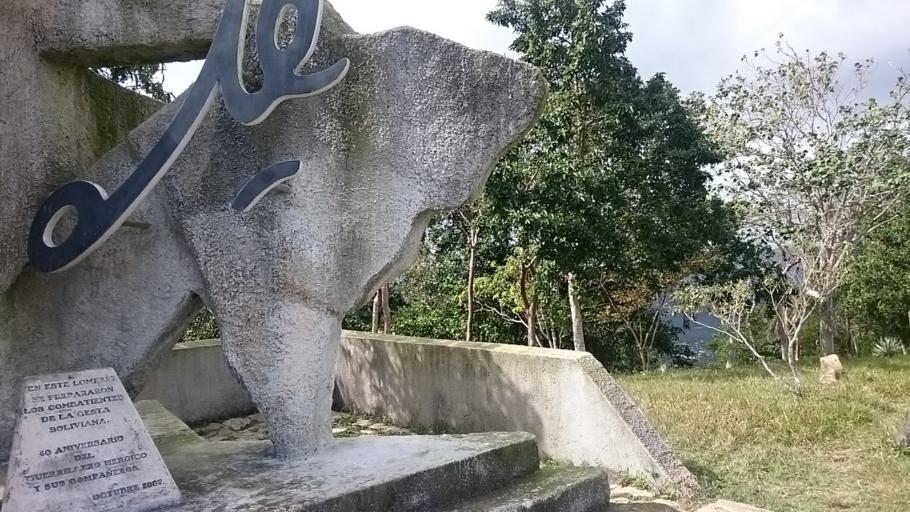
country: CU
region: Artemisa
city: Soroa
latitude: 22.8336
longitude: -82.9265
